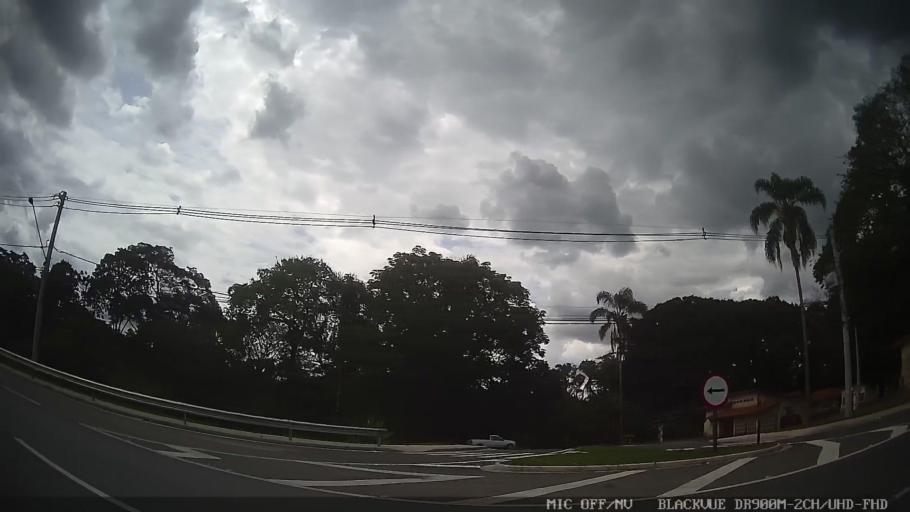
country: BR
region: Sao Paulo
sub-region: Suzano
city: Suzano
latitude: -23.6481
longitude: -46.3246
